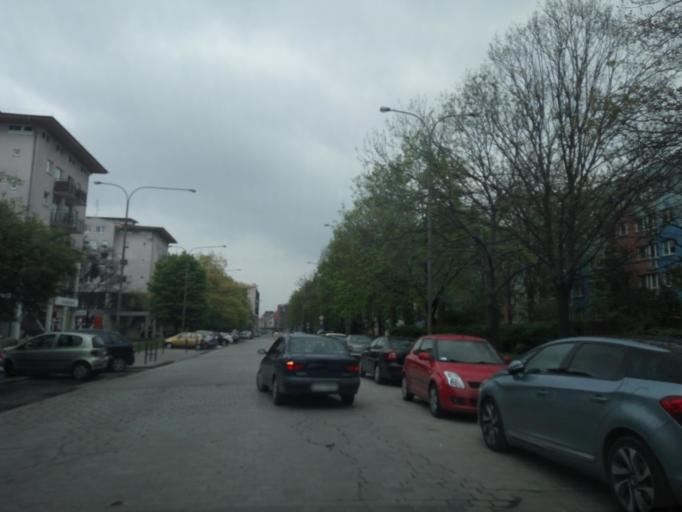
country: PL
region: Lower Silesian Voivodeship
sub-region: Powiat wroclawski
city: Wroclaw
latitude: 51.0963
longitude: 17.0279
